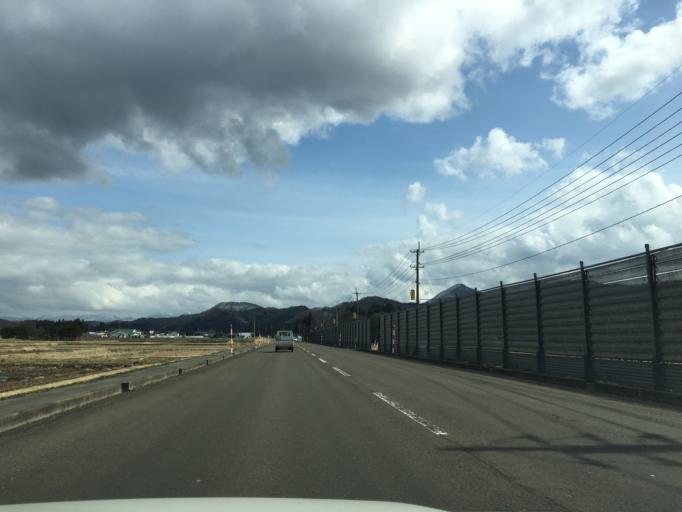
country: JP
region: Akita
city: Odate
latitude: 40.2167
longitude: 140.6177
